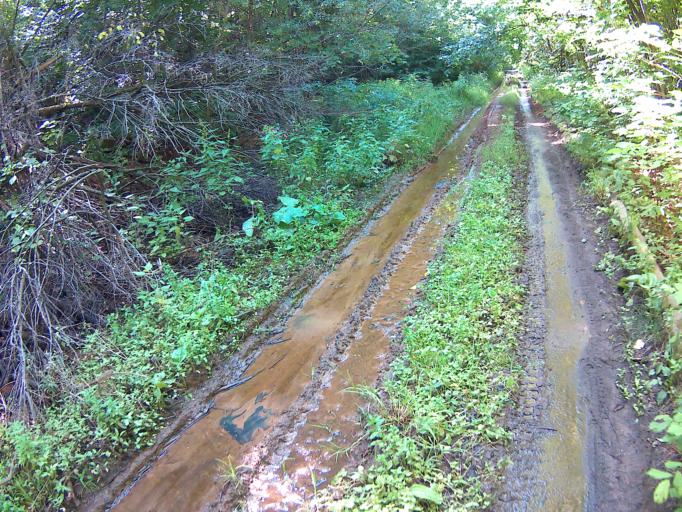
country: RU
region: Nizjnij Novgorod
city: Nizhniy Novgorod
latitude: 56.2337
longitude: 43.9314
